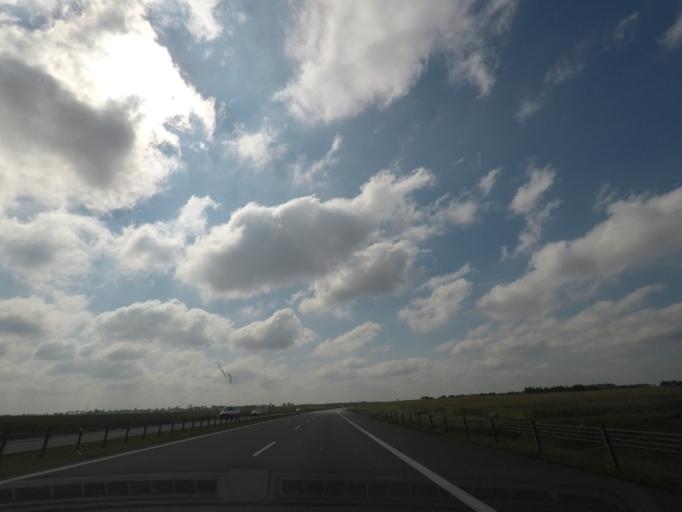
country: PL
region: Kujawsko-Pomorskie
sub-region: Powiat wabrzeski
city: Pluznica
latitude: 53.2178
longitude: 18.7352
